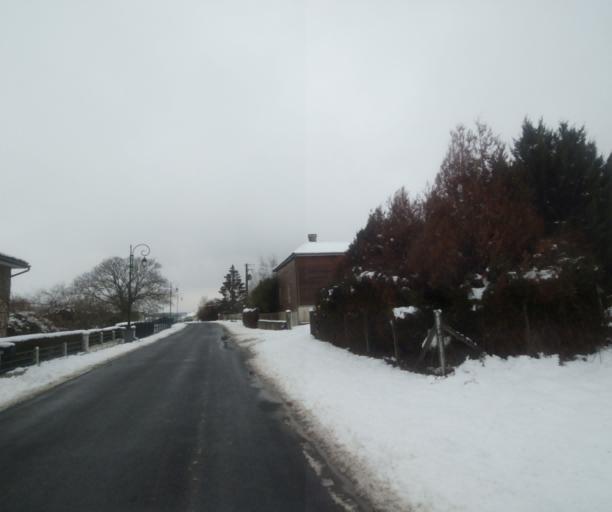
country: FR
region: Champagne-Ardenne
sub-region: Departement de la Haute-Marne
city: Montier-en-Der
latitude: 48.5190
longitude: 4.8195
